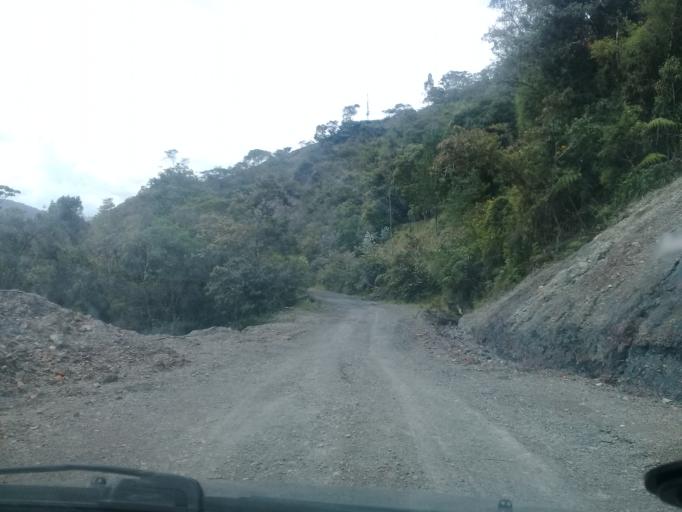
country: CO
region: Cundinamarca
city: Gachala
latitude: 4.7036
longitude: -73.4375
